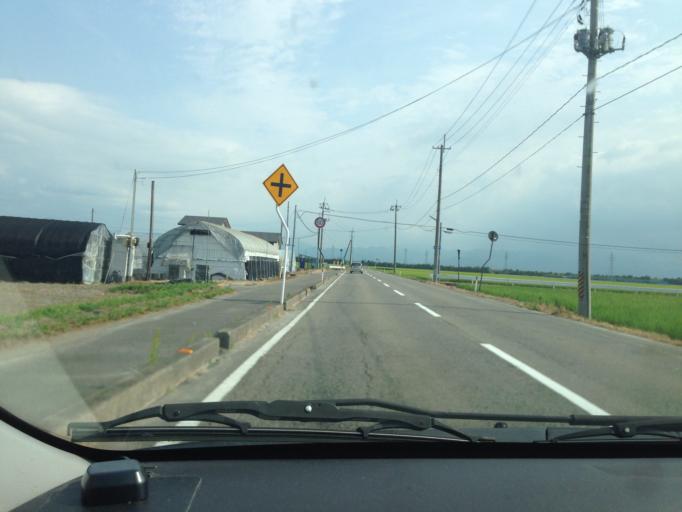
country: JP
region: Fukushima
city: Kitakata
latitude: 37.5389
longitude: 139.8580
